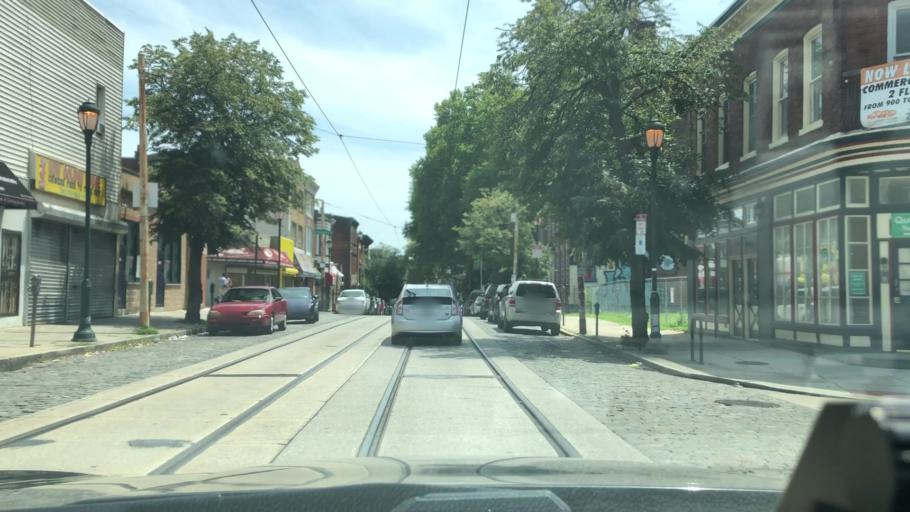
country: US
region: Pennsylvania
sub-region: Montgomery County
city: Wyndmoor
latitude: 40.0378
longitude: -75.1766
